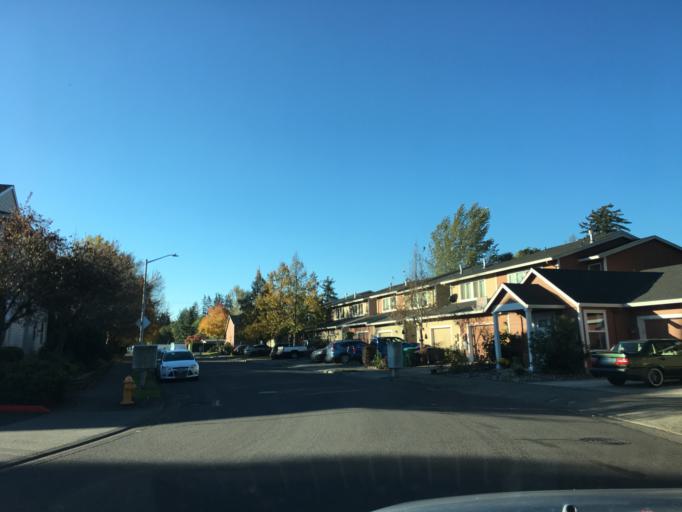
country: US
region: Oregon
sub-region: Multnomah County
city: Gresham
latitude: 45.5061
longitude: -122.4030
